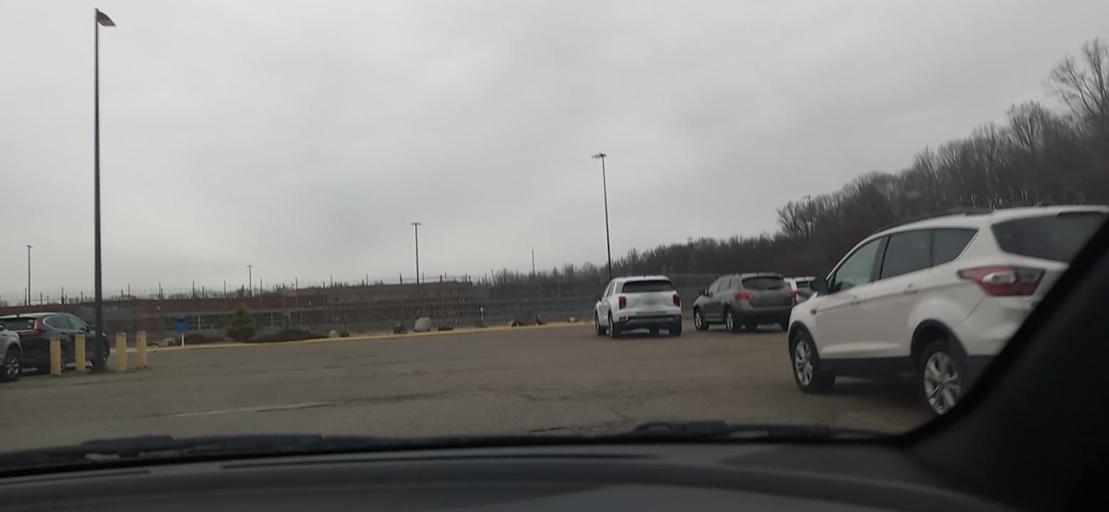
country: US
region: Ohio
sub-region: Trumbull County
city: Leavittsburg
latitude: 41.2329
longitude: -80.8888
